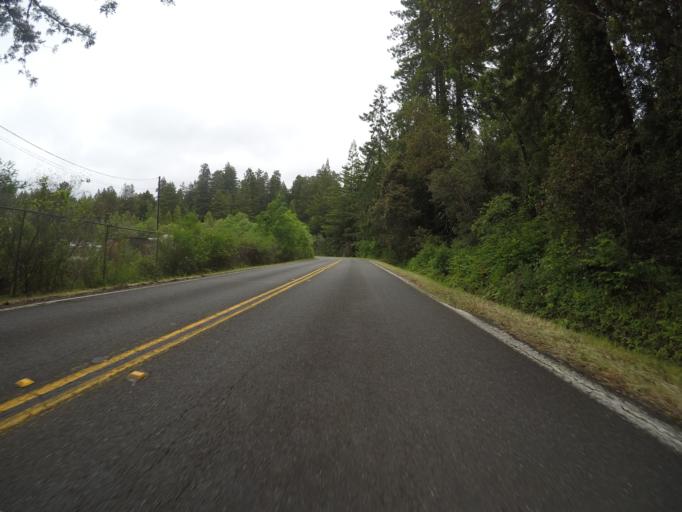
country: US
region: California
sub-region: Humboldt County
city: Rio Dell
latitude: 40.3965
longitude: -123.9405
